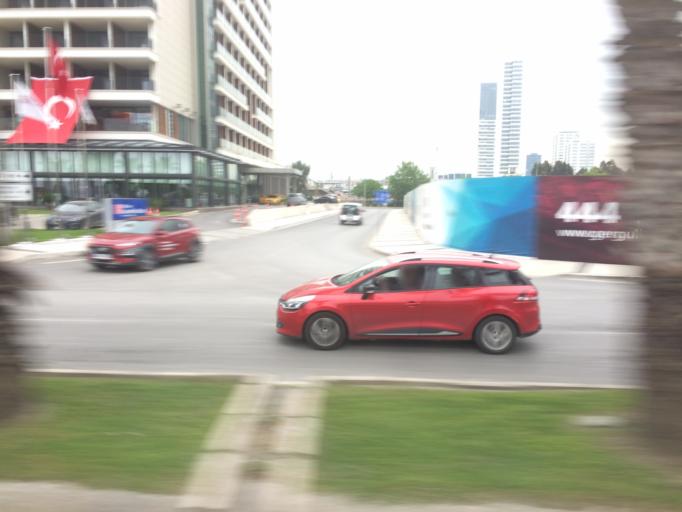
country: TR
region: Izmir
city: Izmir
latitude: 38.4497
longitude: 27.1706
